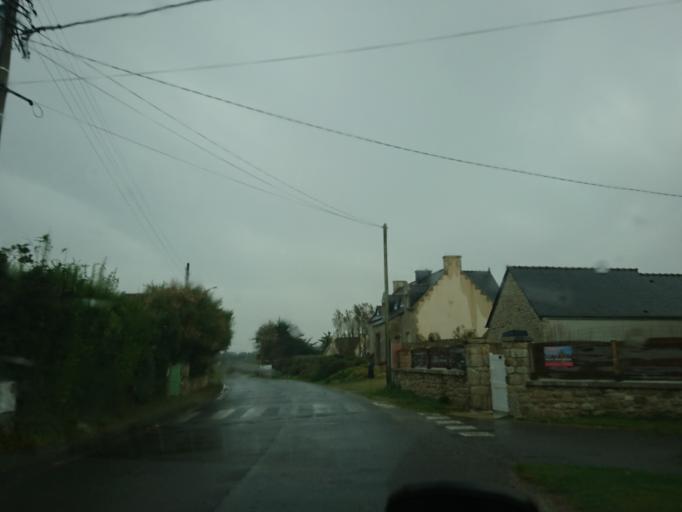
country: FR
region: Brittany
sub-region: Departement du Finistere
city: Guisseny
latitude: 48.6365
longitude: -4.4421
